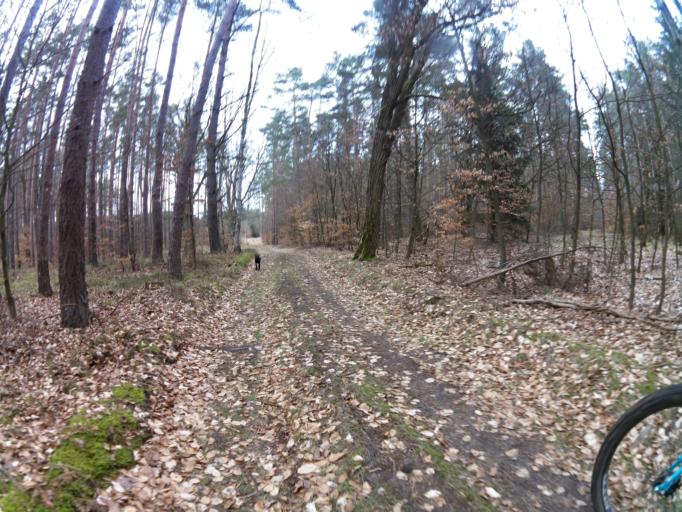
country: PL
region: Lubusz
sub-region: Powiat gorzowski
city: Witnica
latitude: 52.7666
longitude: 14.8305
